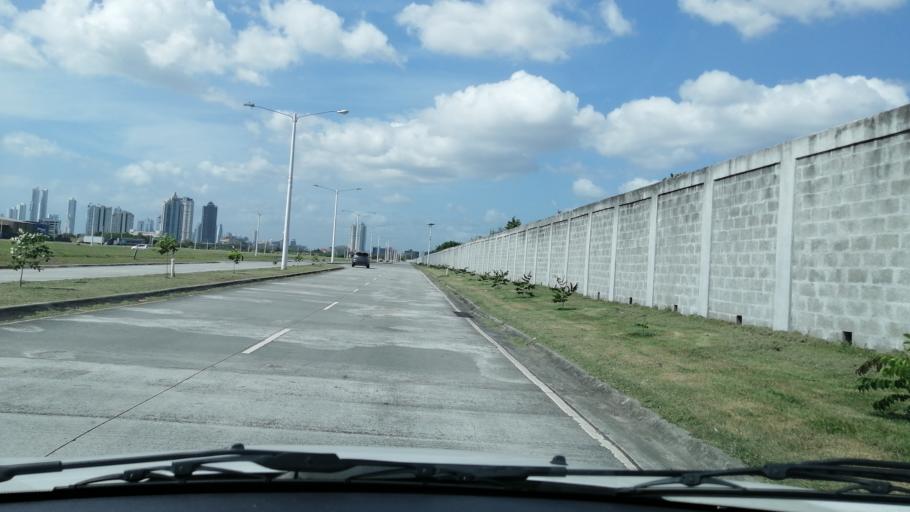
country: PA
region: Panama
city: San Miguelito
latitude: 9.0371
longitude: -79.4396
